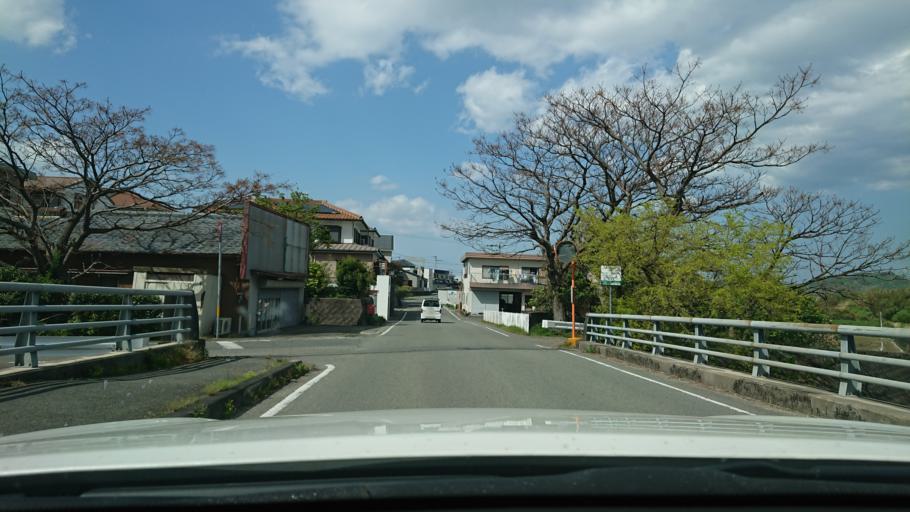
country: JP
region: Tokushima
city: Komatsushimacho
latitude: 34.0006
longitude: 134.5473
